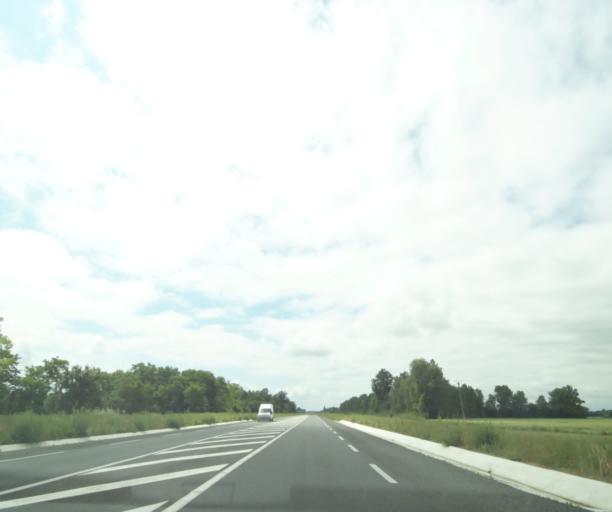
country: FR
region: Pays de la Loire
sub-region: Departement de Maine-et-Loire
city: Montreuil-Bellay
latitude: 47.0790
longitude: -0.1755
